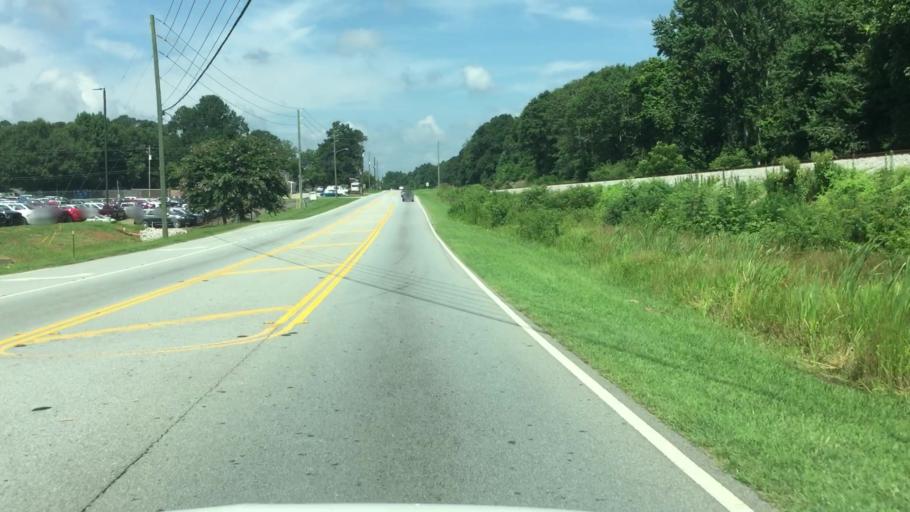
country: US
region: Georgia
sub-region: Barrow County
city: Winder
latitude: 33.9944
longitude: -83.7414
